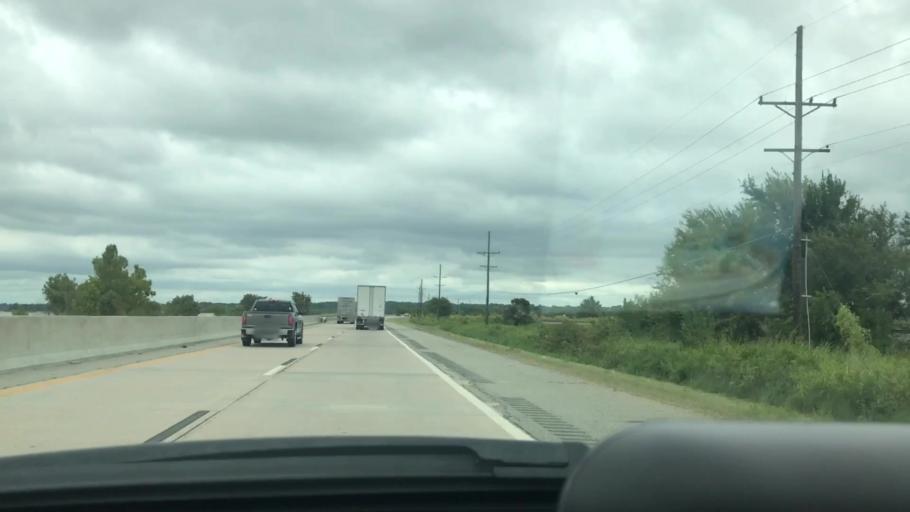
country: US
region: Oklahoma
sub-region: McIntosh County
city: Eufaula
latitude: 35.3347
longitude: -95.5866
